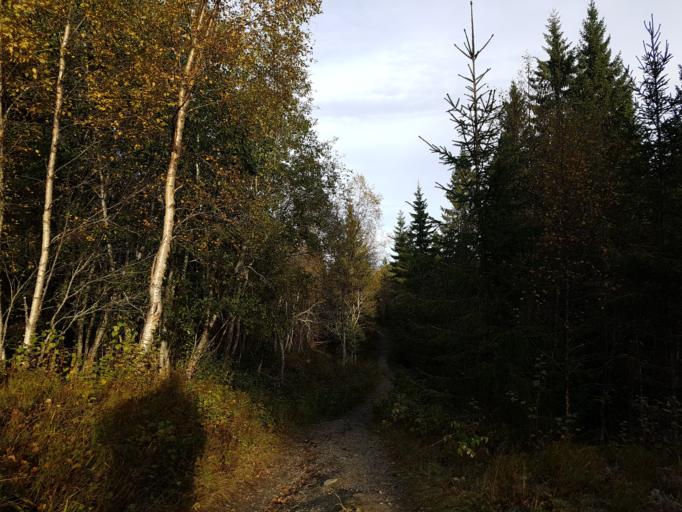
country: NO
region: Sor-Trondelag
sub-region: Trondheim
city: Trondheim
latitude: 63.4429
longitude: 10.2912
